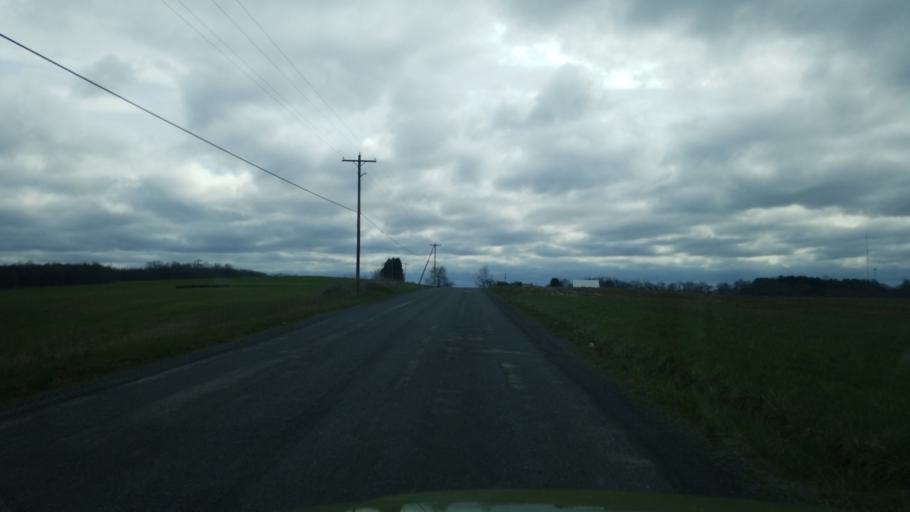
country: US
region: Pennsylvania
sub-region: Clearfield County
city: Clearfield
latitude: 41.0784
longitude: -78.3809
